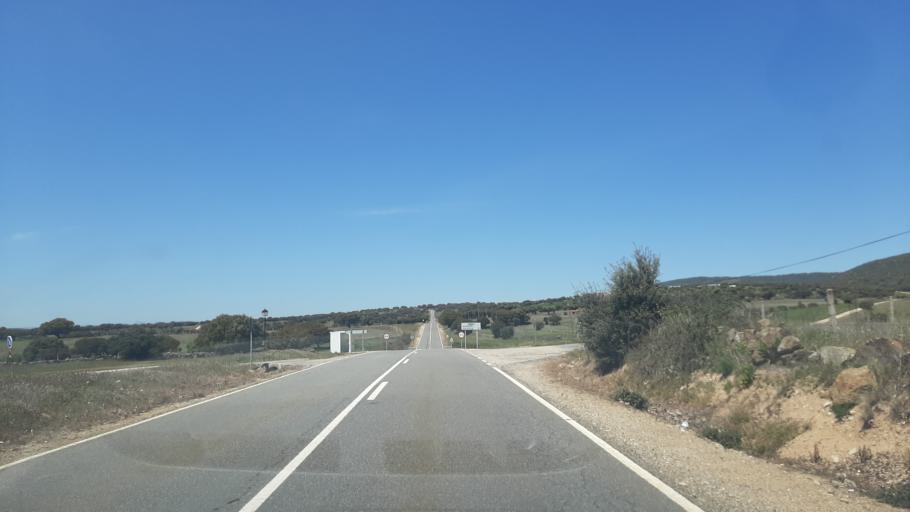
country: ES
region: Castille and Leon
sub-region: Provincia de Salamanca
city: Puente del Congosto
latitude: 40.5239
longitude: -5.5006
